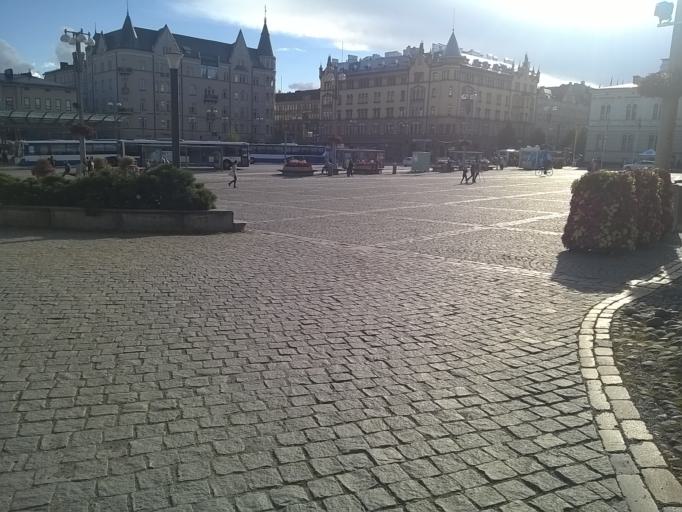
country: FI
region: Pirkanmaa
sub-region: Tampere
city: Tampere
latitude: 61.4984
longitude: 23.7618
